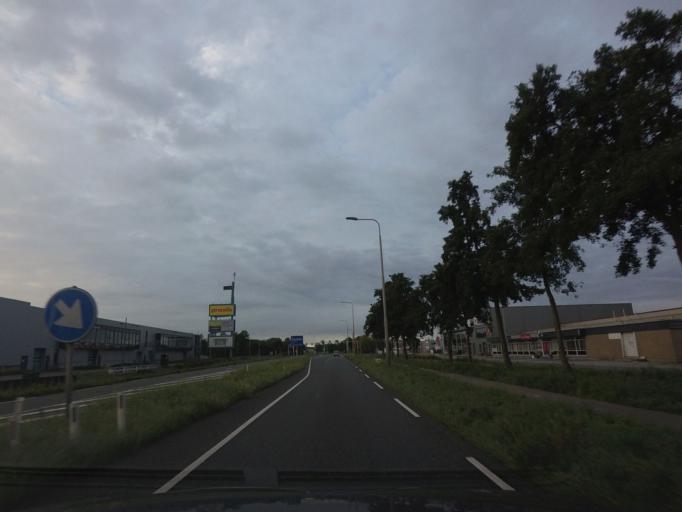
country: NL
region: North Holland
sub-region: Gemeente Zaanstad
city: Zaanstad
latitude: 52.5061
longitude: 4.7790
